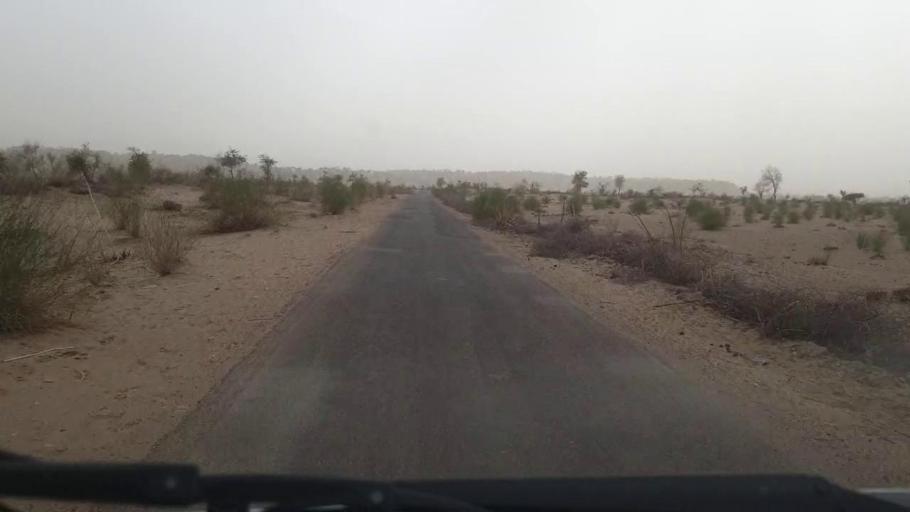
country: PK
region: Sindh
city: Islamkot
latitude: 25.0676
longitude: 70.5546
